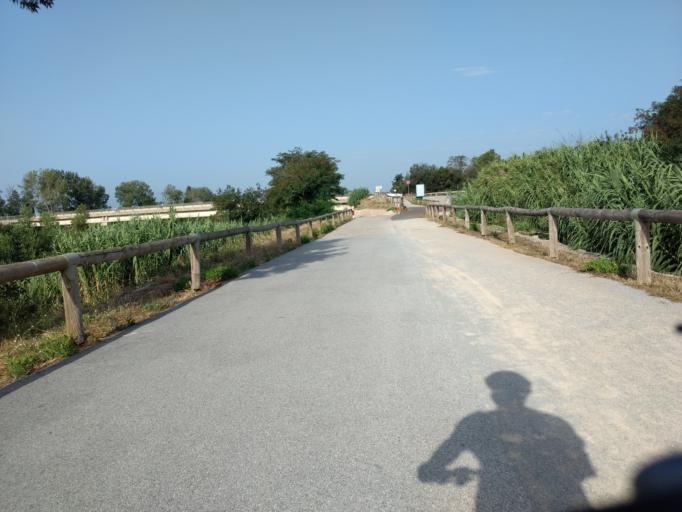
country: FR
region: Languedoc-Roussillon
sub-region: Departement des Pyrenees-Orientales
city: Claira
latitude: 42.7530
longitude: 2.9546
